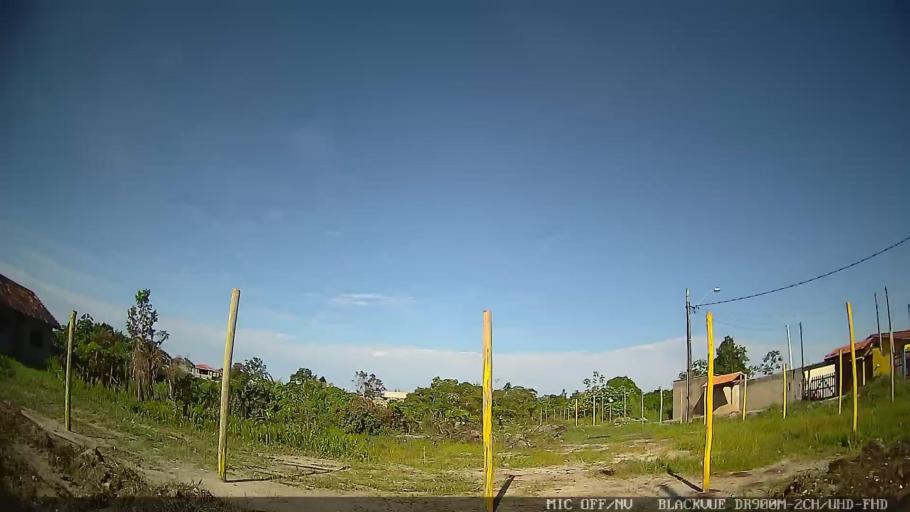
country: BR
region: Sao Paulo
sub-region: Itanhaem
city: Itanhaem
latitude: -24.2234
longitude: -46.8812
